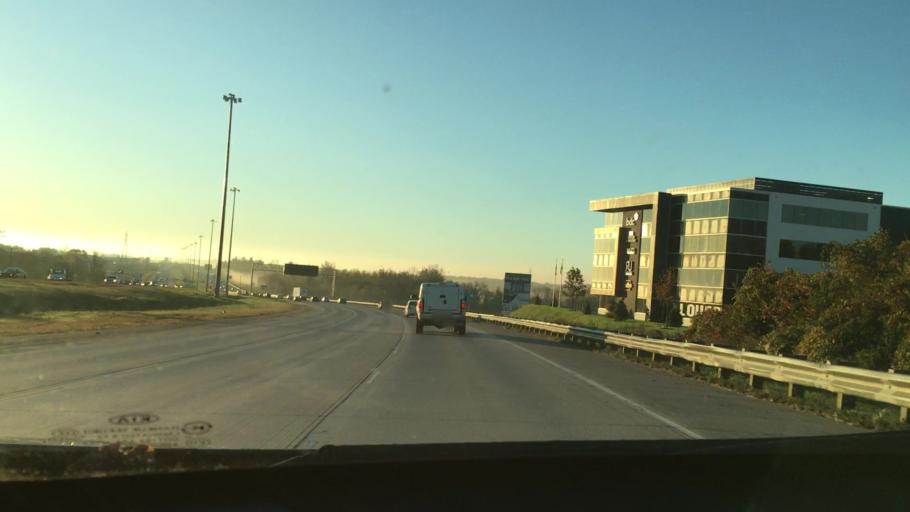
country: CA
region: Quebec
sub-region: Laurentides
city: Saint-Jerome
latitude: 45.7559
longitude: -74.0193
